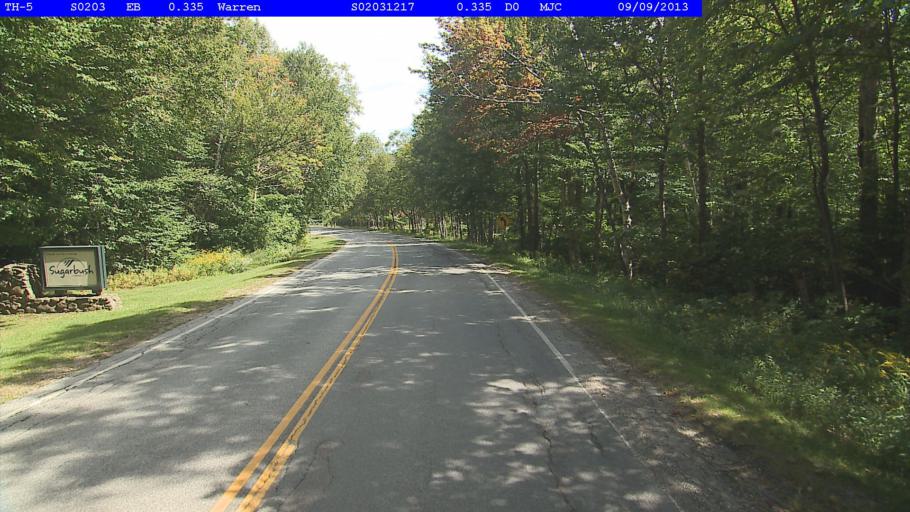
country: US
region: Vermont
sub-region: Addison County
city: Bristol
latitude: 44.1367
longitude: -72.8889
